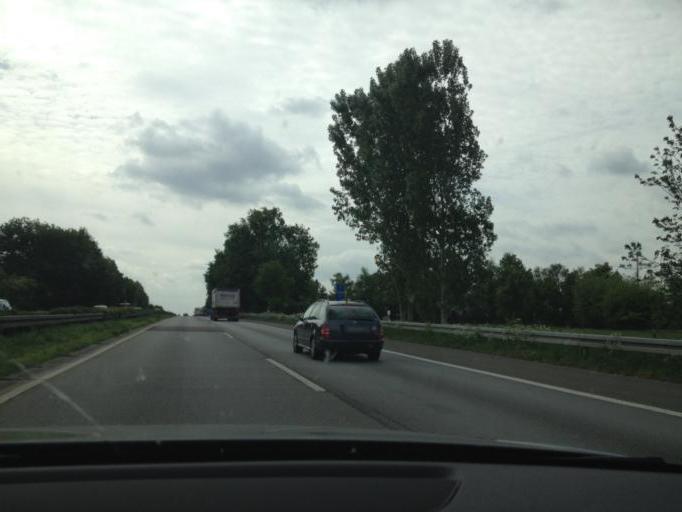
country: DE
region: North Rhine-Westphalia
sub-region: Regierungsbezirk Dusseldorf
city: Dinslaken
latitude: 51.5672
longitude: 6.8036
